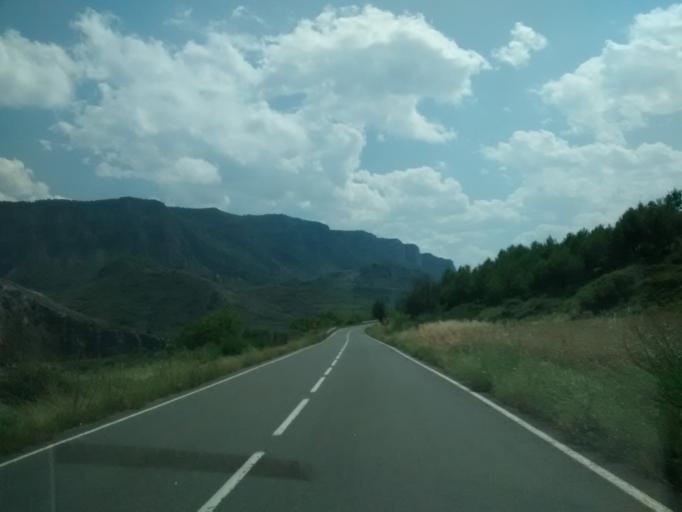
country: ES
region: La Rioja
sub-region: Provincia de La Rioja
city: Leza de Rio Leza
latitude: 42.3465
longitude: -2.3945
